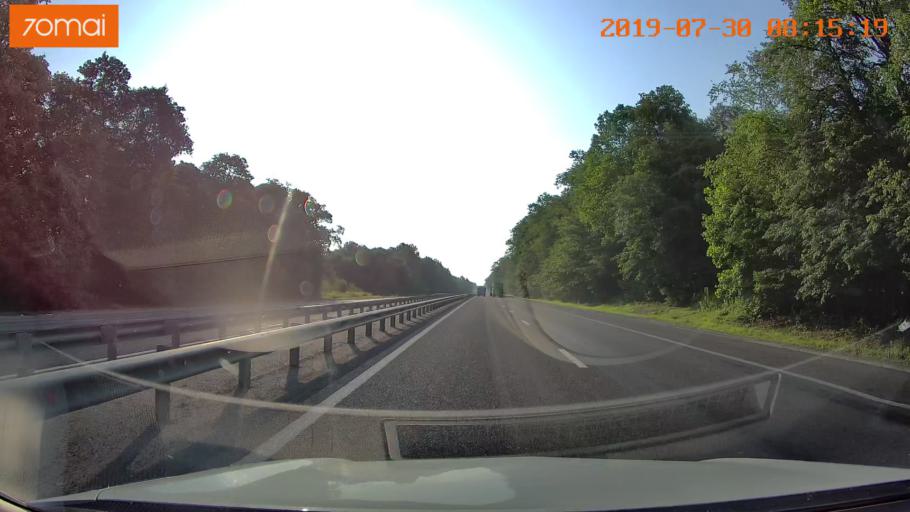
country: RU
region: Kaliningrad
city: Zheleznodorozhnyy
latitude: 54.6450
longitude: 21.3825
